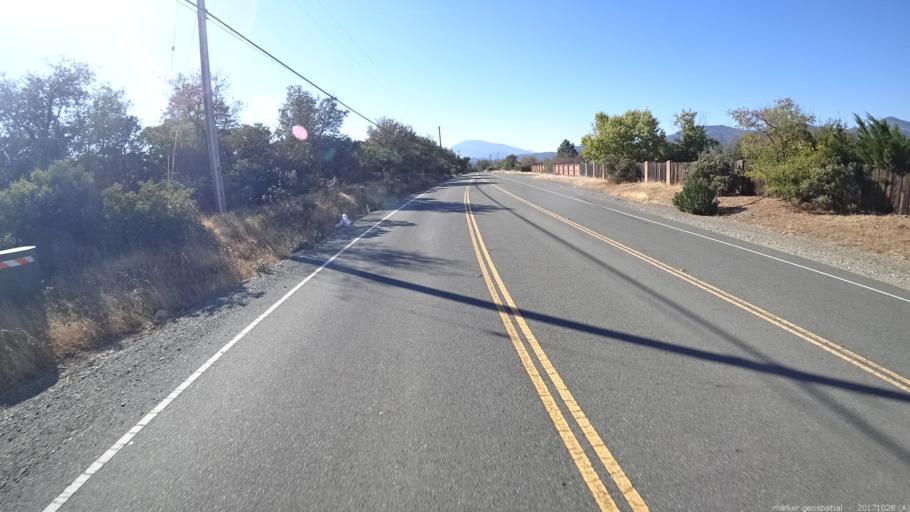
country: US
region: California
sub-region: Shasta County
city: Redding
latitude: 40.6151
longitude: -122.4322
